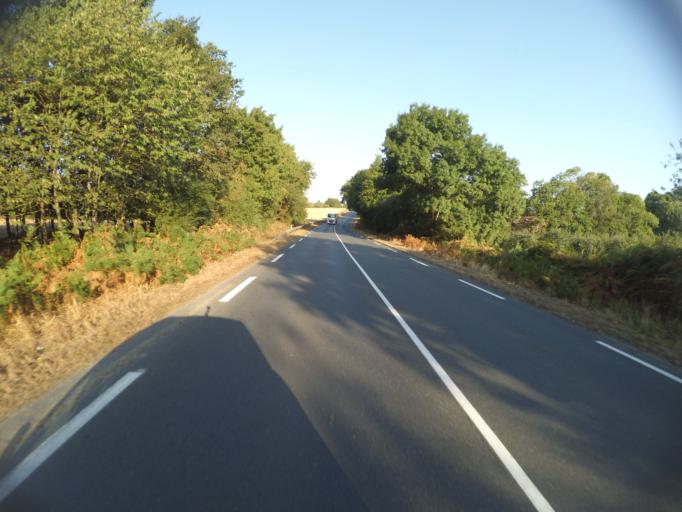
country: FR
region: Pays de la Loire
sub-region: Departement de la Loire-Atlantique
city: Remouille
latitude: 47.0637
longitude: -1.3859
